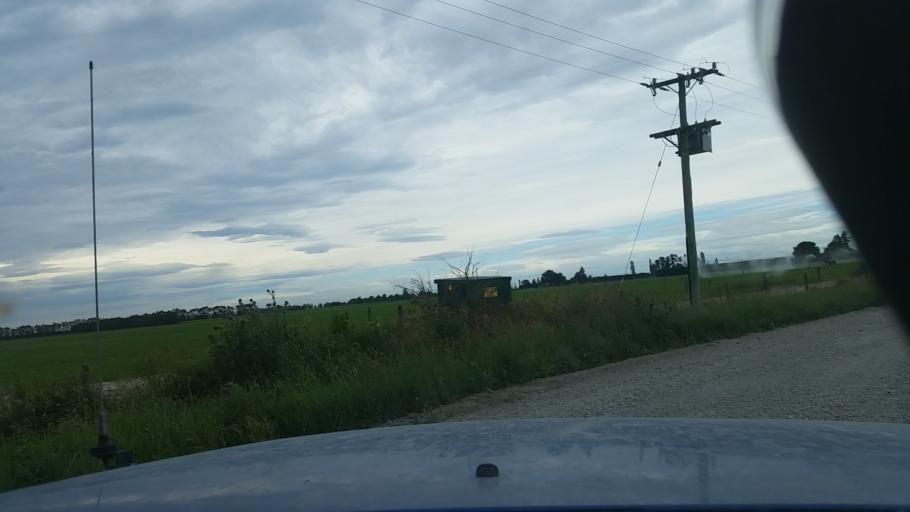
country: NZ
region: Canterbury
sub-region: Ashburton District
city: Ashburton
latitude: -43.8581
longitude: 171.6626
